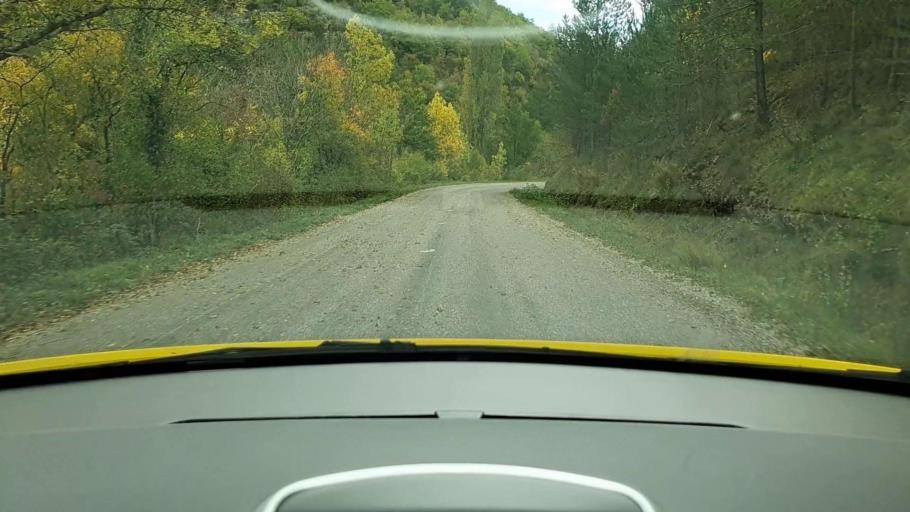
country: FR
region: Languedoc-Roussillon
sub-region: Departement de la Lozere
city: Meyrueis
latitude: 44.0774
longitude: 3.3539
